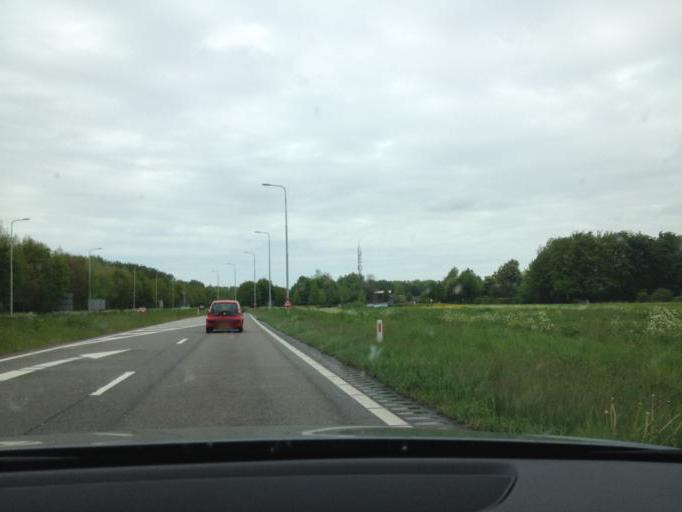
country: NL
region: North Holland
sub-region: Gemeente Huizen
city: Huizen
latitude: 52.3393
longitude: 5.2674
